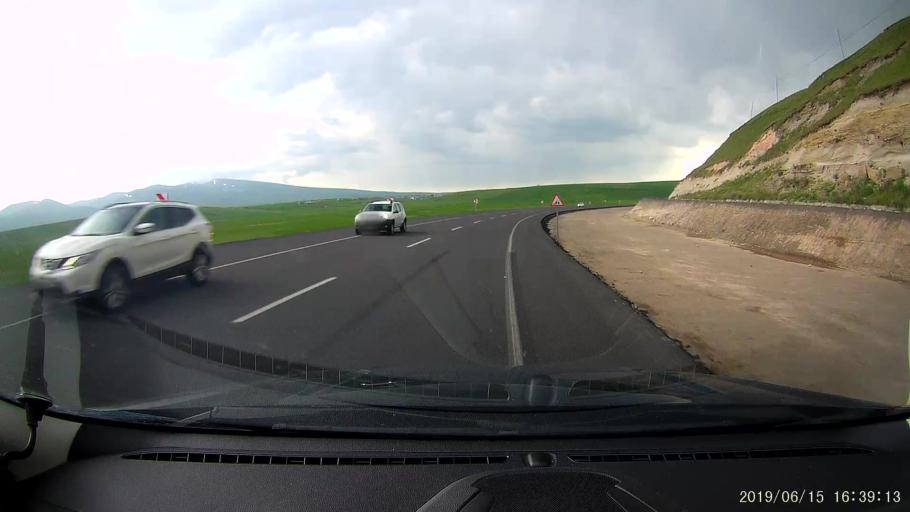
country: TR
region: Ardahan
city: Haskoy
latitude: 40.9853
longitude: 42.8954
